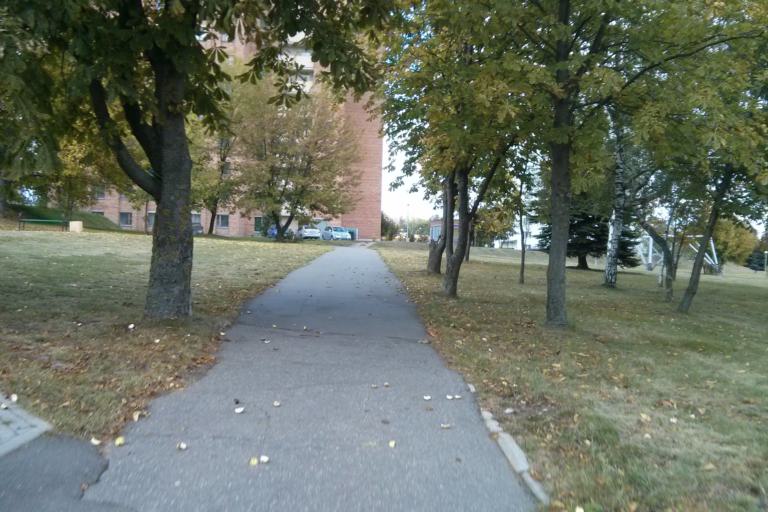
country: BY
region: Minsk
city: Minsk
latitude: 53.8785
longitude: 27.5981
